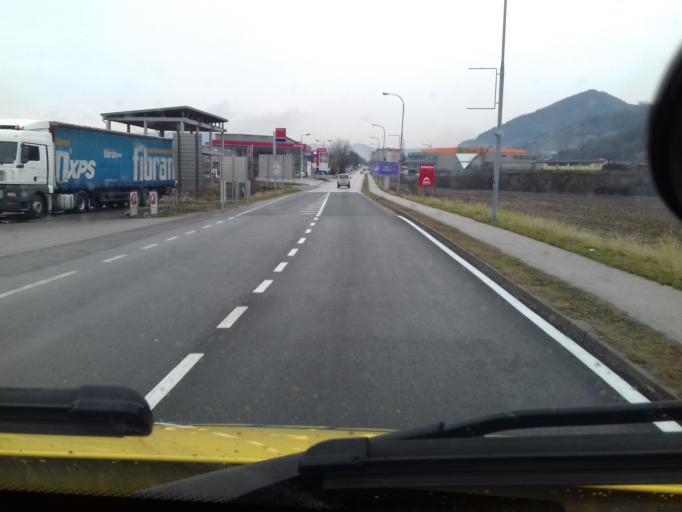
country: BA
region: Federation of Bosnia and Herzegovina
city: Visoko
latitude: 43.9993
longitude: 18.1671
